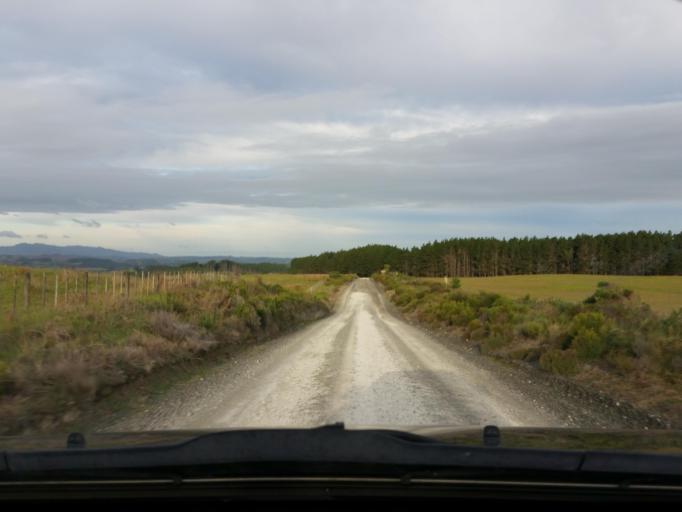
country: NZ
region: Northland
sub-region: Kaipara District
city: Dargaville
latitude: -35.9115
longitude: 173.7428
